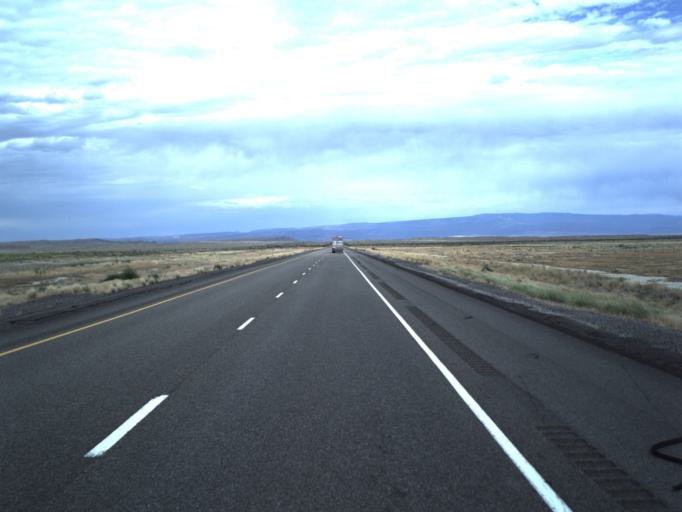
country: US
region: Utah
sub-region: Grand County
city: Moab
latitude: 38.9418
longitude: -109.5799
